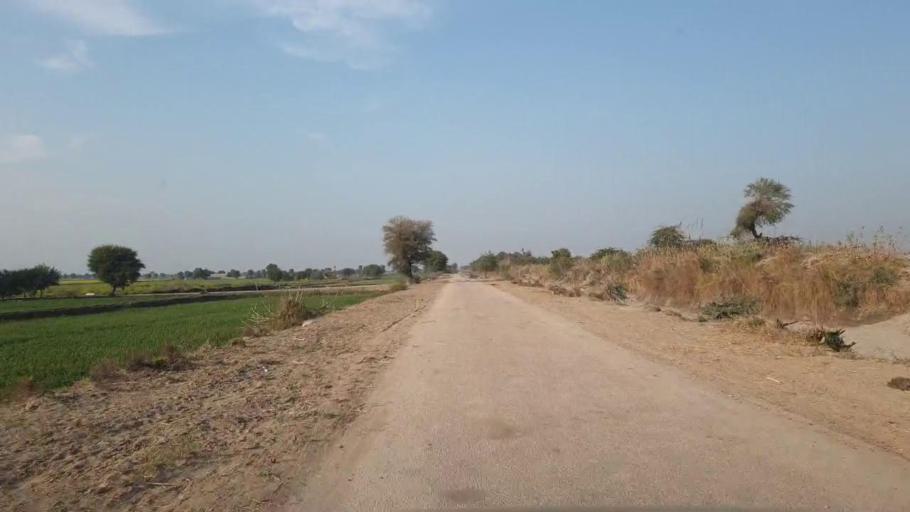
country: PK
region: Sindh
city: Shahpur Chakar
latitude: 26.1646
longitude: 68.6405
